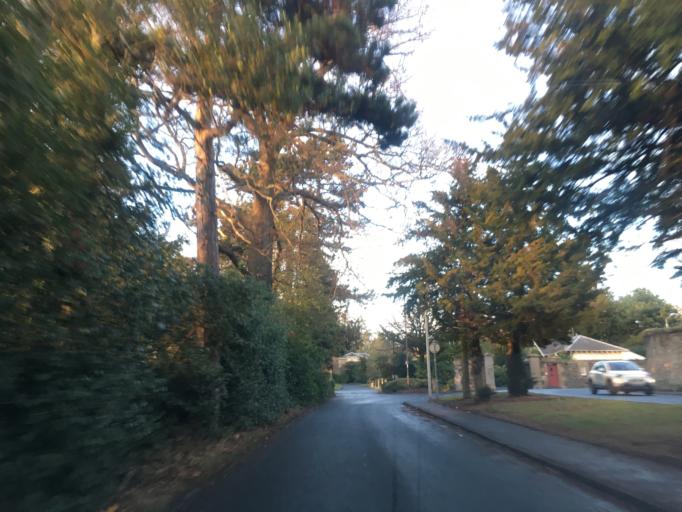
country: GB
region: Scotland
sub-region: Edinburgh
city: Colinton
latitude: 55.9455
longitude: -3.2513
